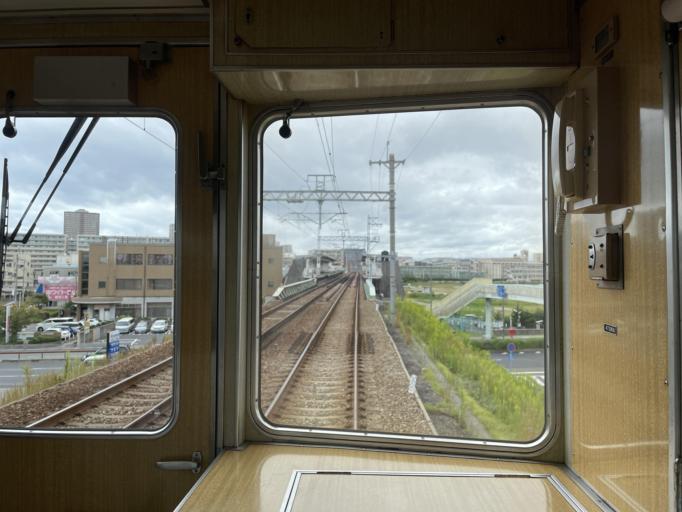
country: JP
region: Hyogo
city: Nishinomiya-hama
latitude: 34.7365
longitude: 135.3543
